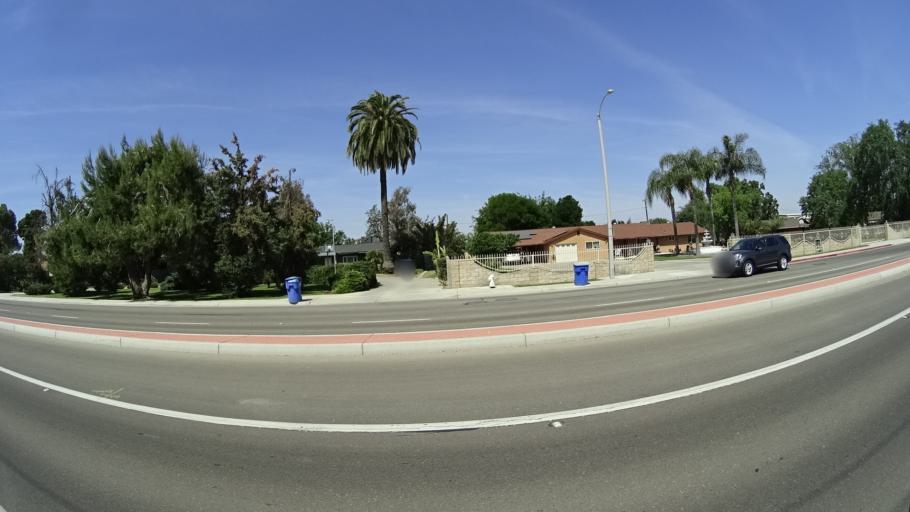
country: US
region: California
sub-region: Kings County
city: Hanford
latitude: 36.3468
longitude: -119.6728
